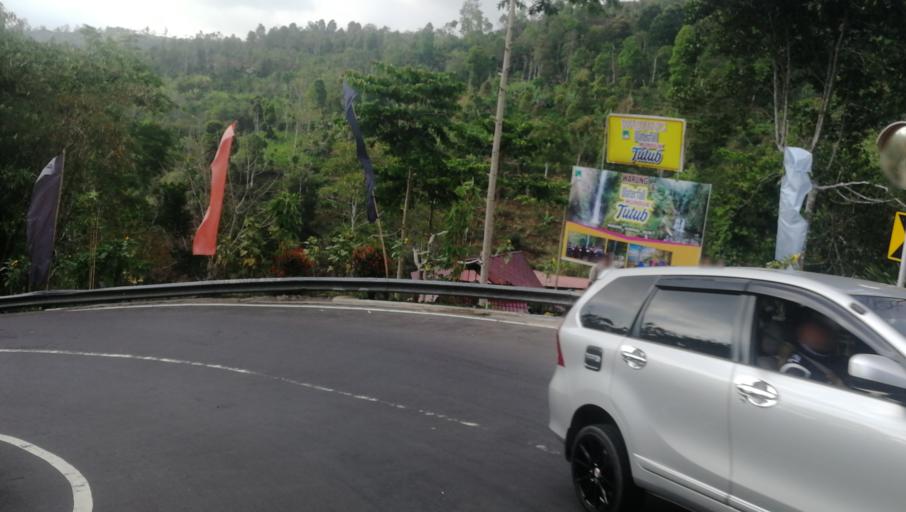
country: ID
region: Bali
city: Munduk
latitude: -8.2546
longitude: 115.0792
